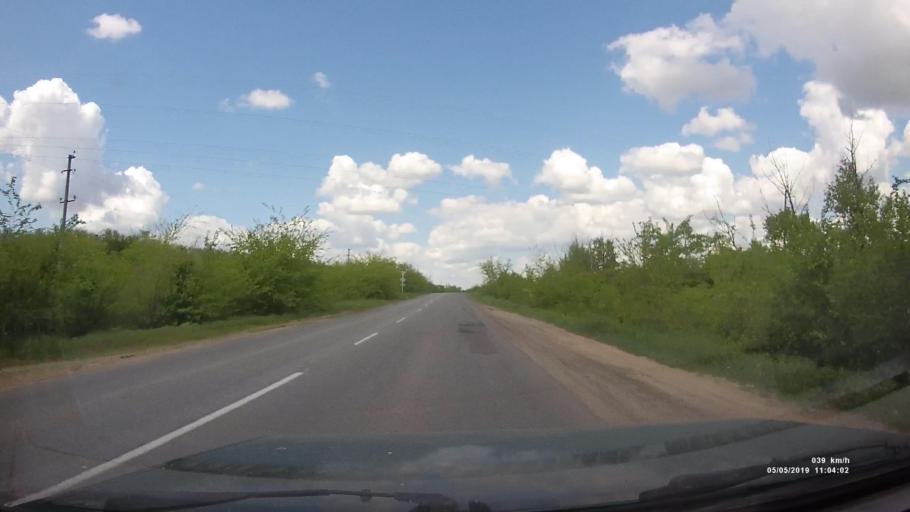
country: RU
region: Rostov
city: Ust'-Donetskiy
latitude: 47.6948
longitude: 40.9224
